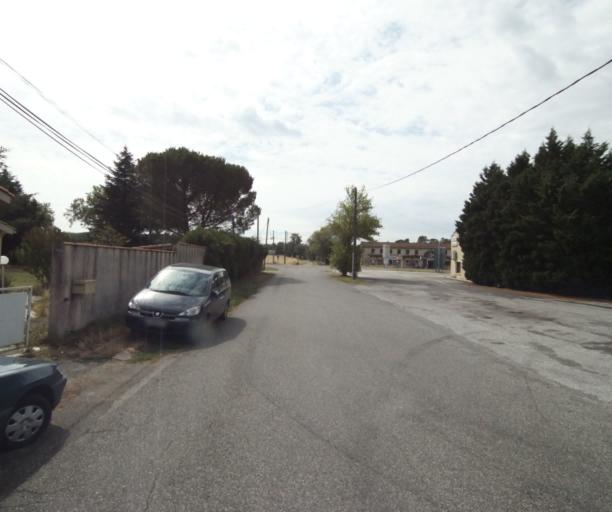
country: FR
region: Midi-Pyrenees
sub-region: Departement de la Haute-Garonne
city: Revel
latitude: 43.4483
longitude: 1.9618
